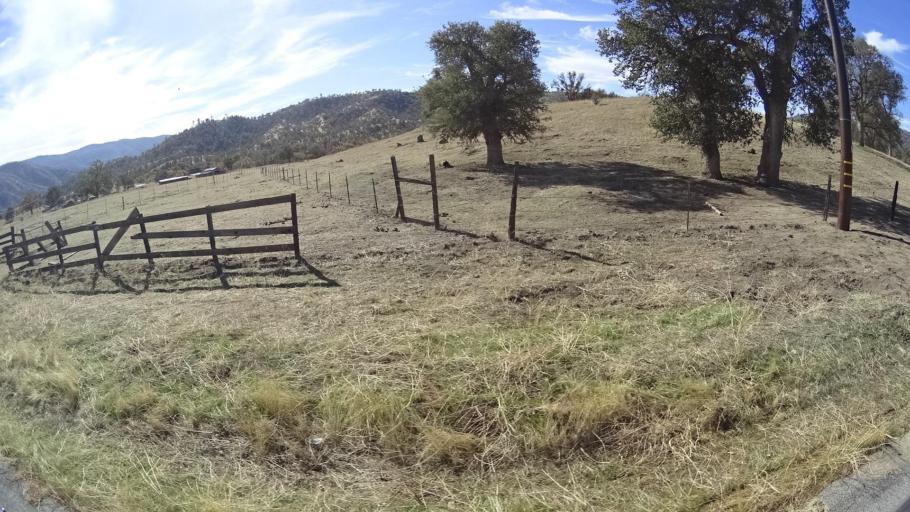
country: US
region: California
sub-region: Kern County
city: Alta Sierra
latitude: 35.6195
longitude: -118.7330
